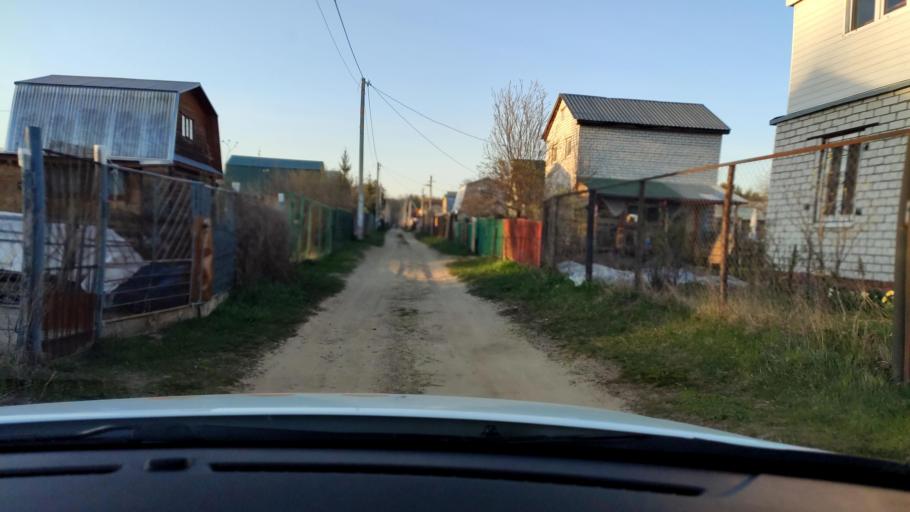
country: RU
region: Tatarstan
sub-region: Gorod Kazan'
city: Kazan
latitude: 55.9216
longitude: 49.1481
